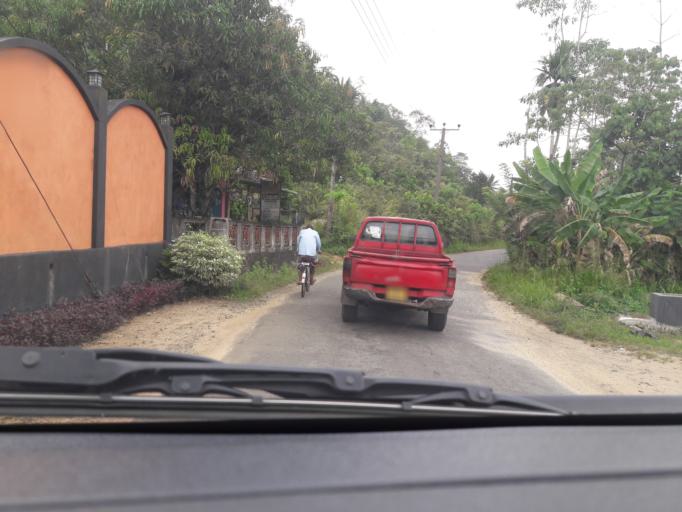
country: LK
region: Southern
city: Hikkaduwa
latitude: 6.2520
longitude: 80.2670
